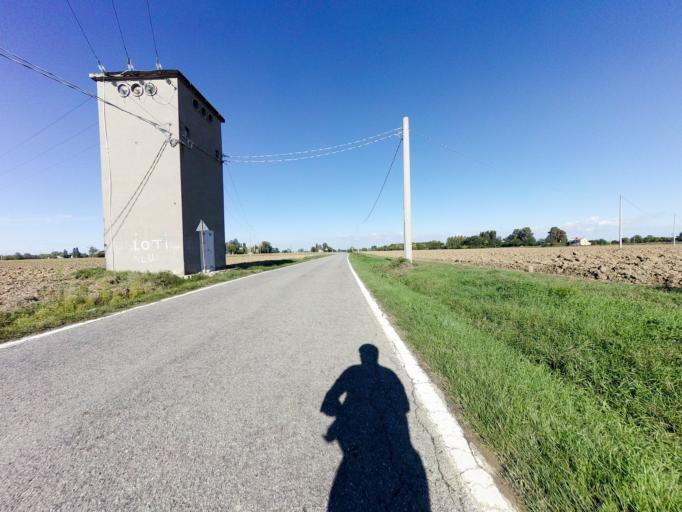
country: IT
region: Emilia-Romagna
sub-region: Provincia di Bologna
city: Progresso
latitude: 44.5601
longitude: 11.3905
